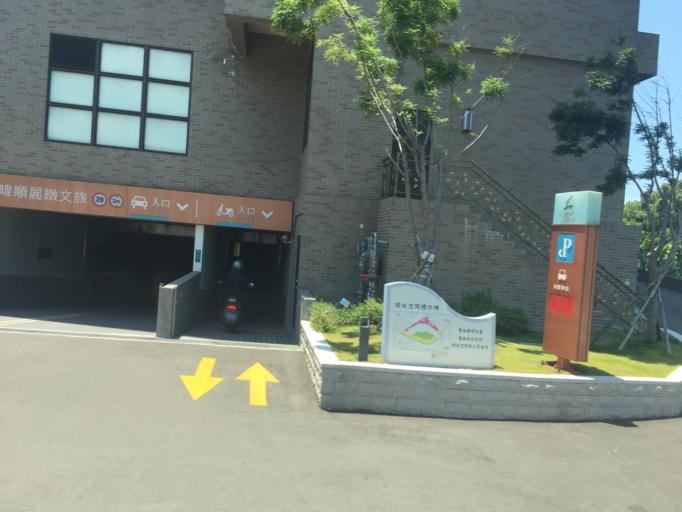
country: TW
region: Taiwan
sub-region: Hsinchu
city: Hsinchu
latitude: 24.7893
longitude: 121.0036
